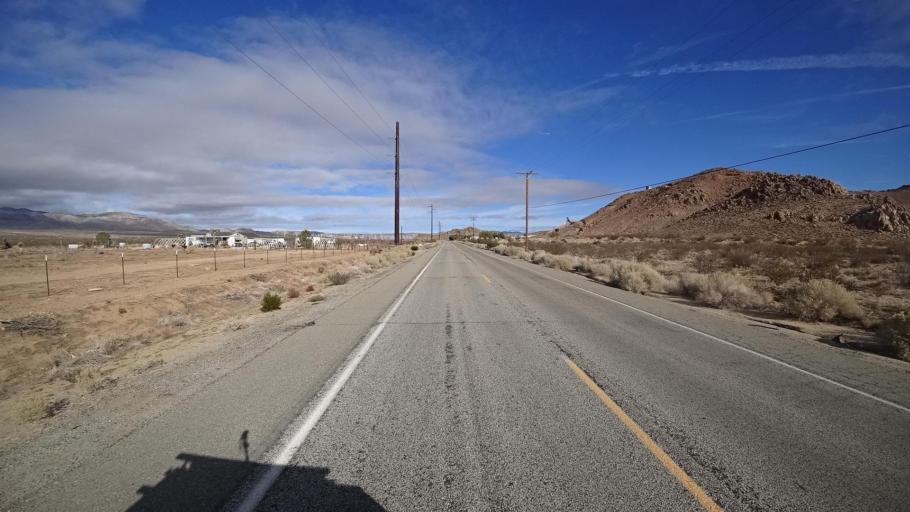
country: US
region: California
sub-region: Kern County
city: Mojave
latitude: 34.9519
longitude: -118.2915
